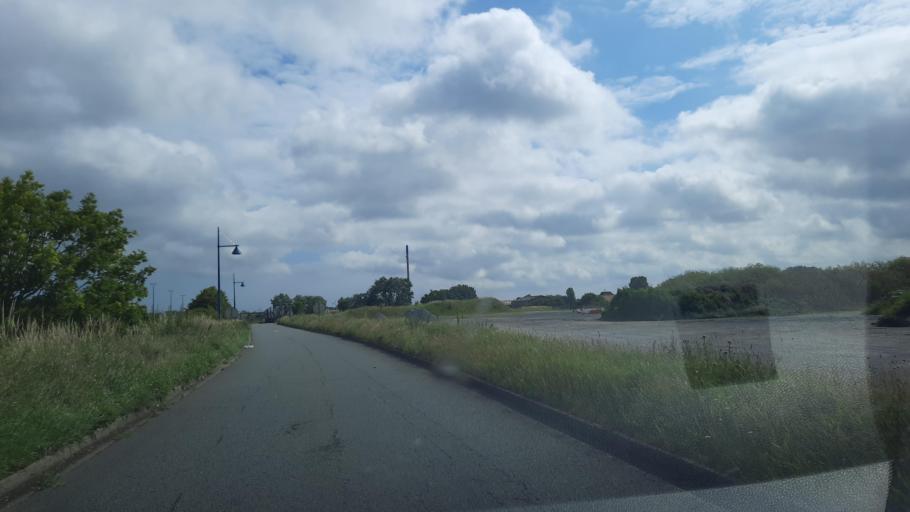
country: FR
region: Nord-Pas-de-Calais
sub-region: Departement du Nord
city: Coudekerque-Village
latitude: 51.0248
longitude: 2.4200
